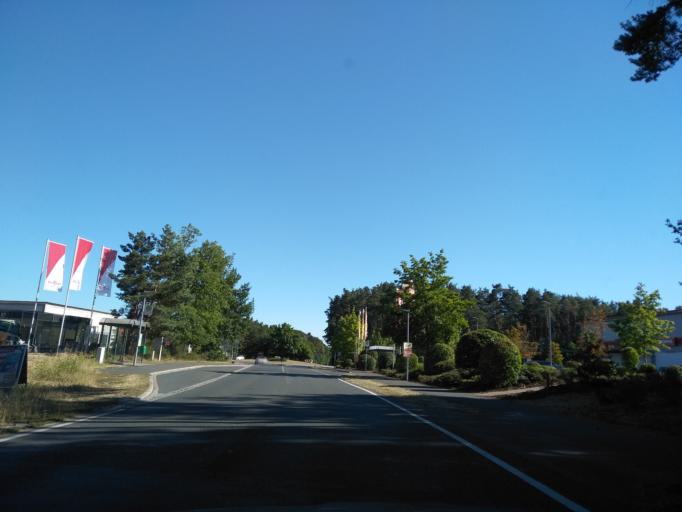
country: DE
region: Bavaria
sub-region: Regierungsbezirk Mittelfranken
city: Rottenbach
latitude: 49.6618
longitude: 10.9181
